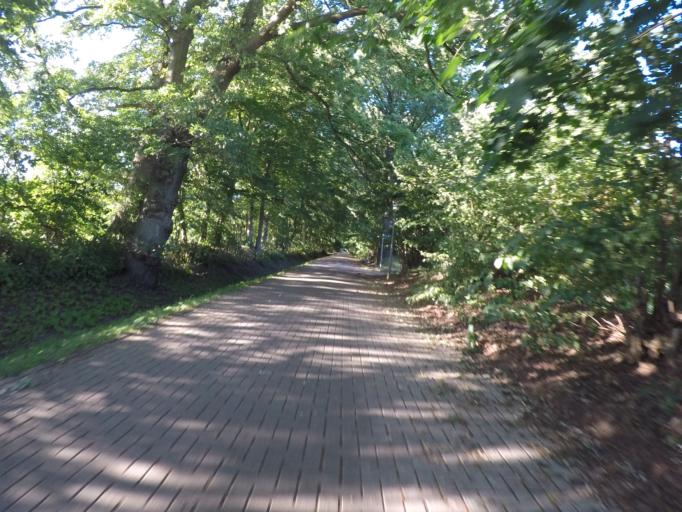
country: DE
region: Hamburg
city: Bergstedt
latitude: 53.6736
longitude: 10.1128
